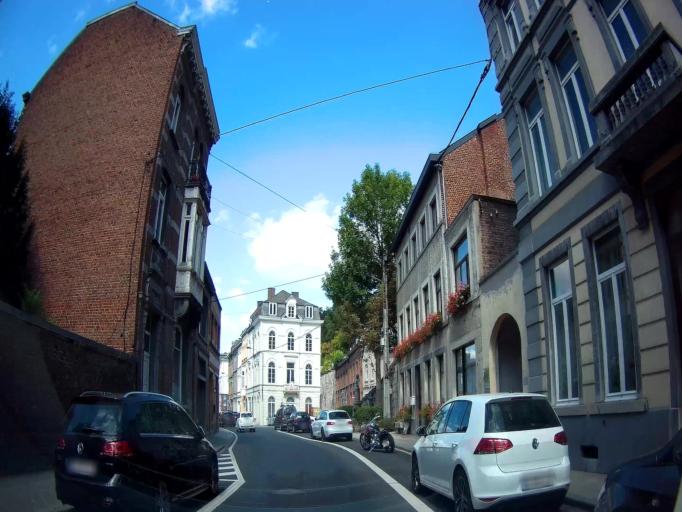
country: BE
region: Wallonia
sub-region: Province de Namur
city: Dinant
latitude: 50.2544
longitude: 4.9172
